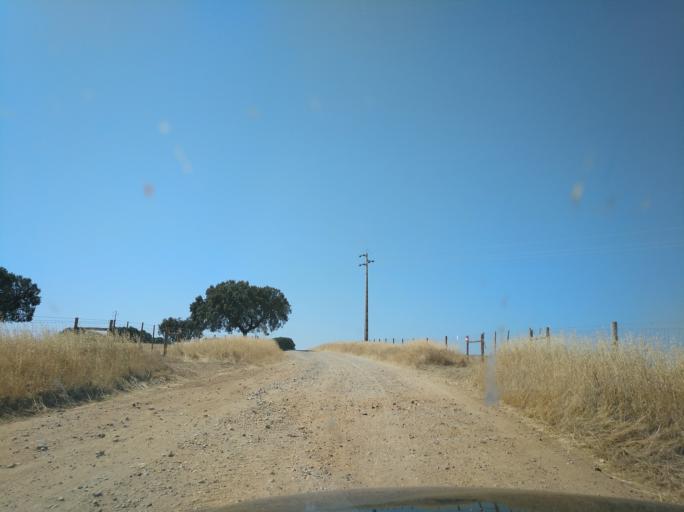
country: PT
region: Portalegre
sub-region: Campo Maior
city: Campo Maior
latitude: 39.0188
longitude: -6.9817
